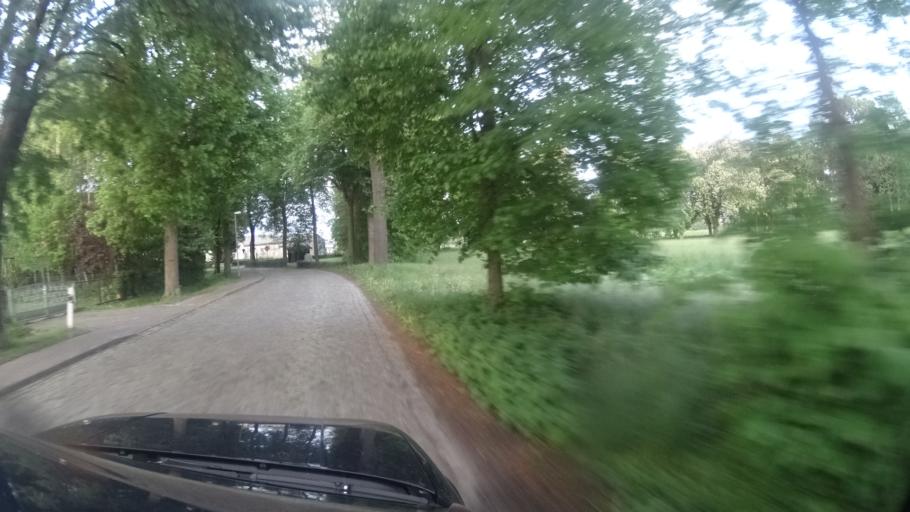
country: DE
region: Brandenburg
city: Ruthnick
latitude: 52.8206
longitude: 12.9598
